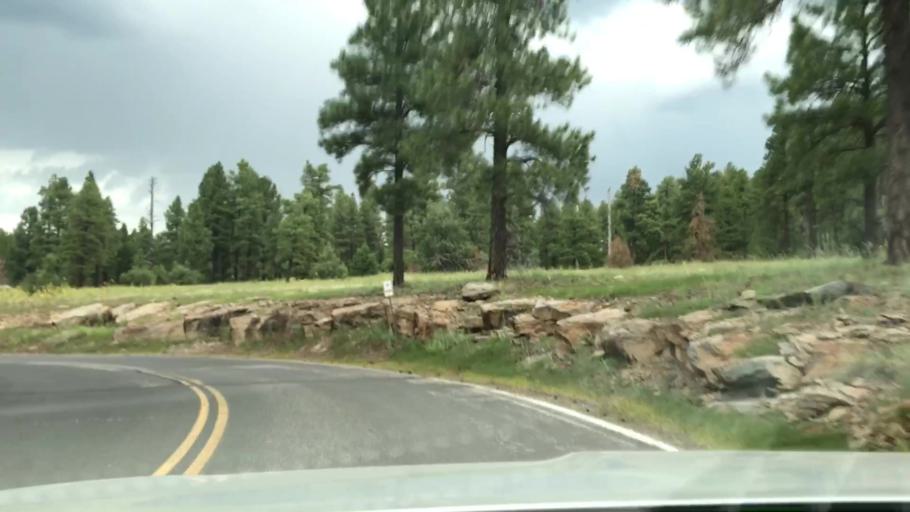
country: US
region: Arizona
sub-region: Coconino County
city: Kachina Village
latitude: 35.0317
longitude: -111.7334
